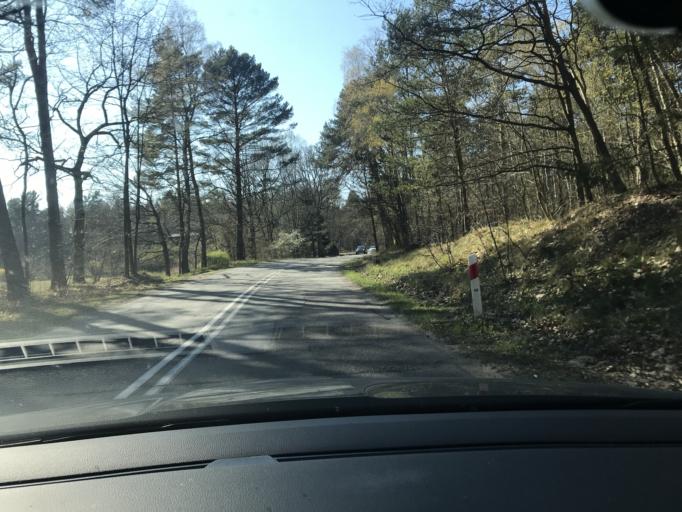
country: PL
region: Pomeranian Voivodeship
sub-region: Powiat nowodworski
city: Sztutowo
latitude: 54.3360
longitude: 19.2105
